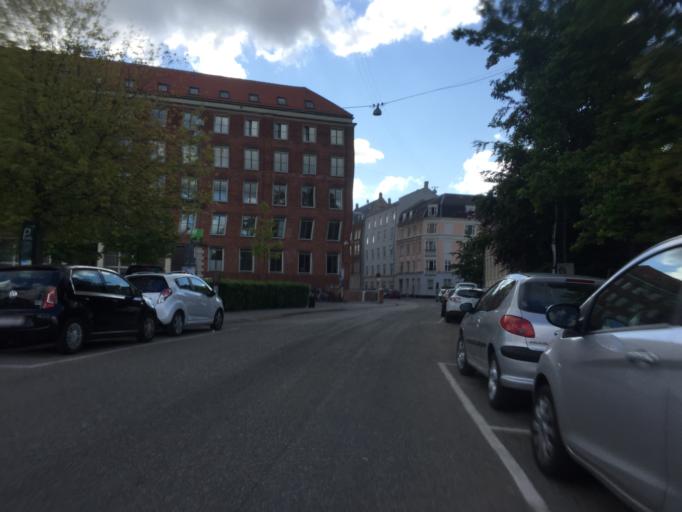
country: DK
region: Capital Region
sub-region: Frederiksberg Kommune
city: Frederiksberg
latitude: 55.6784
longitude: 12.5293
